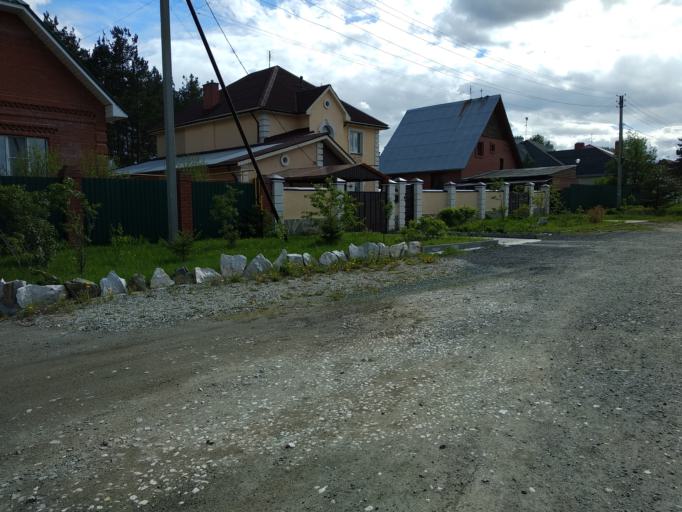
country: RU
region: Sverdlovsk
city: Beryozovsky
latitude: 56.9172
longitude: 60.8199
